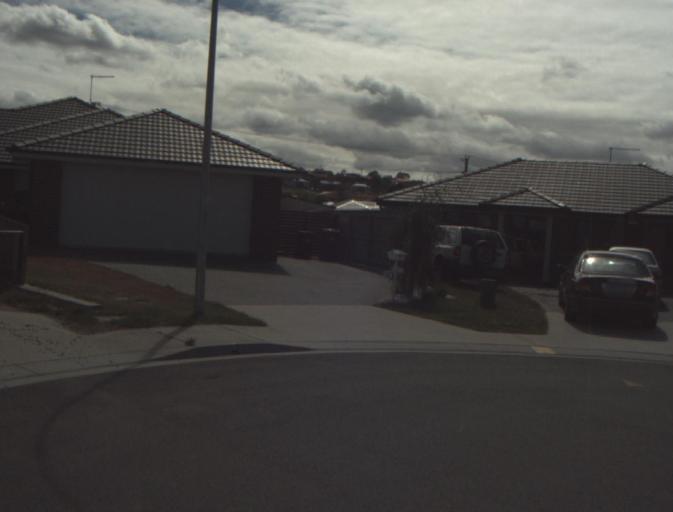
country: AU
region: Tasmania
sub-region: Launceston
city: Mayfield
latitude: -41.3838
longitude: 147.1098
